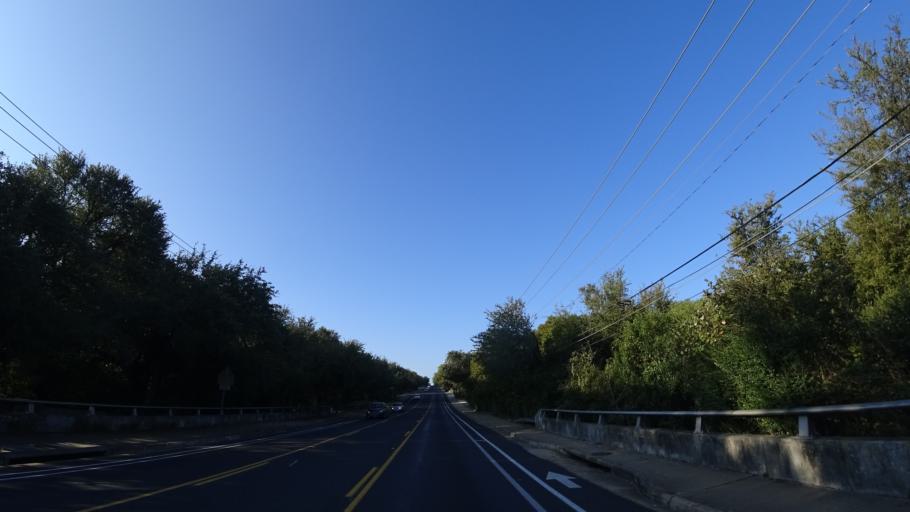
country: US
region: Texas
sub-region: Travis County
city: Rollingwood
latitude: 30.2680
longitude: -97.8054
